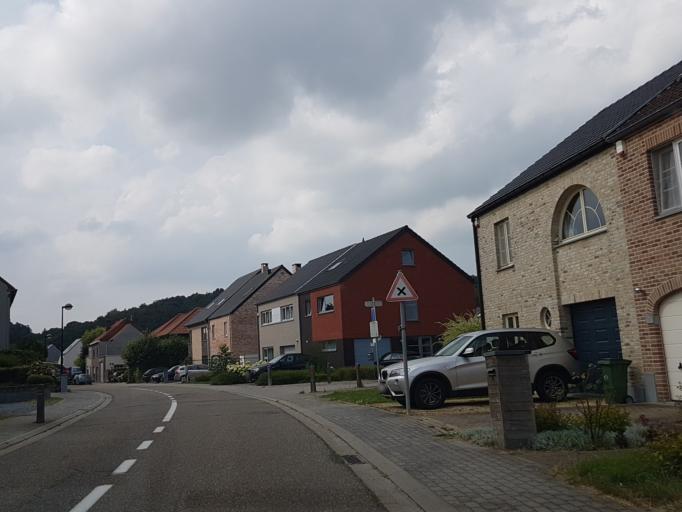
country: BE
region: Flanders
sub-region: Provincie Vlaams-Brabant
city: Kortenberg
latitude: 50.8770
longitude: 4.5525
